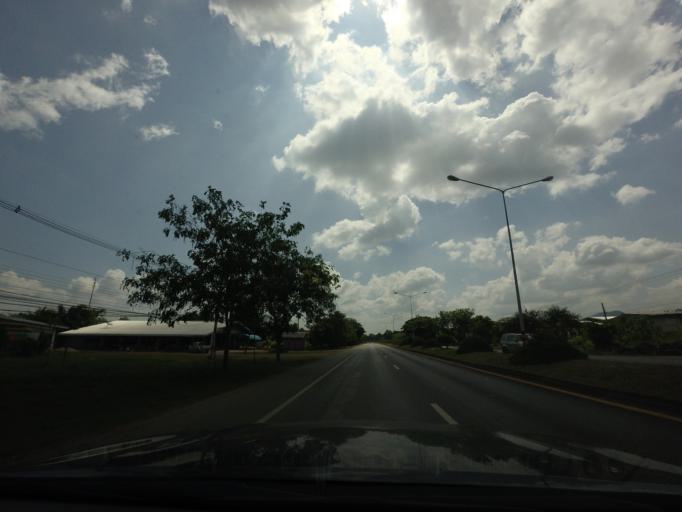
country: TH
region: Phetchabun
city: Nong Phai
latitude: 16.1236
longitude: 101.0399
